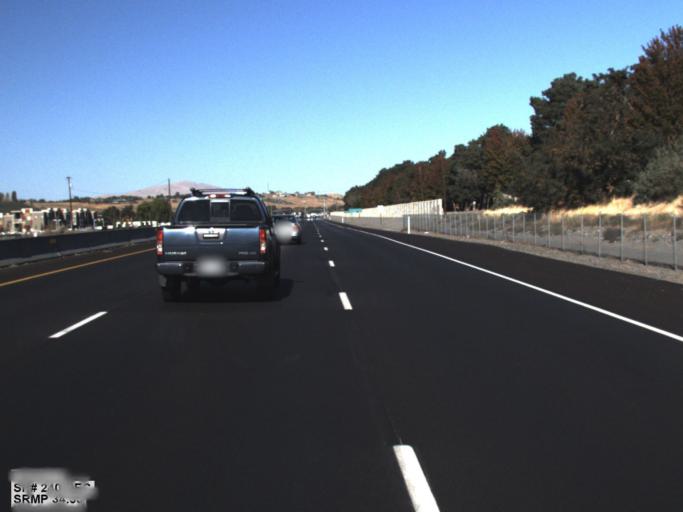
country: US
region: Washington
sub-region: Benton County
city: Richland
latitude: 46.2636
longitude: -119.2946
